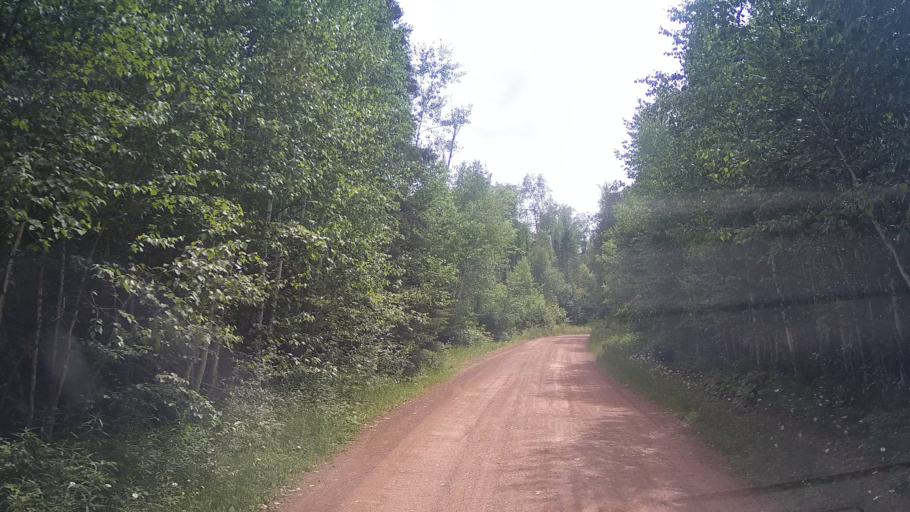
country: CA
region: Ontario
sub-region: Thunder Bay District
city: Thunder Bay
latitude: 48.6799
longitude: -88.6656
